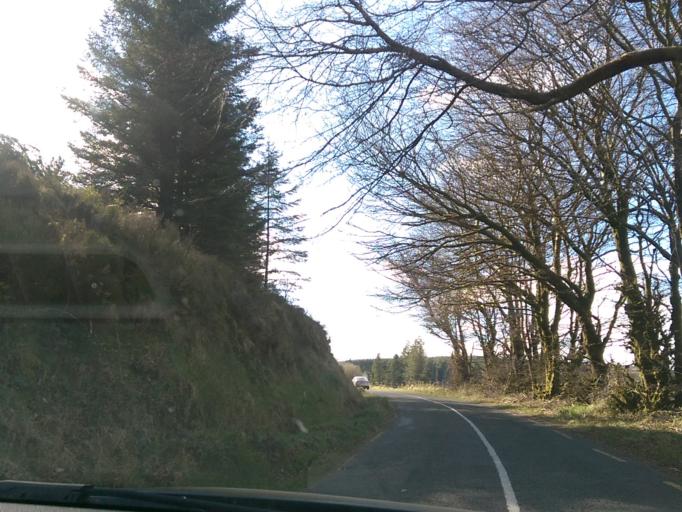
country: IE
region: Leinster
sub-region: Laois
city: Mountrath
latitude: 53.0726
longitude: -7.5781
